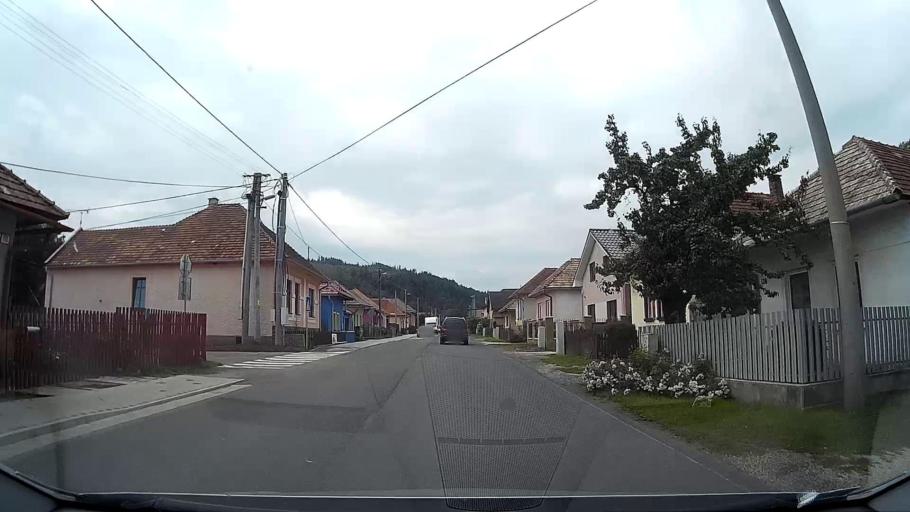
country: SK
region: Presovsky
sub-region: Okres Poprad
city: Poprad
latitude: 48.9843
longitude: 20.3063
